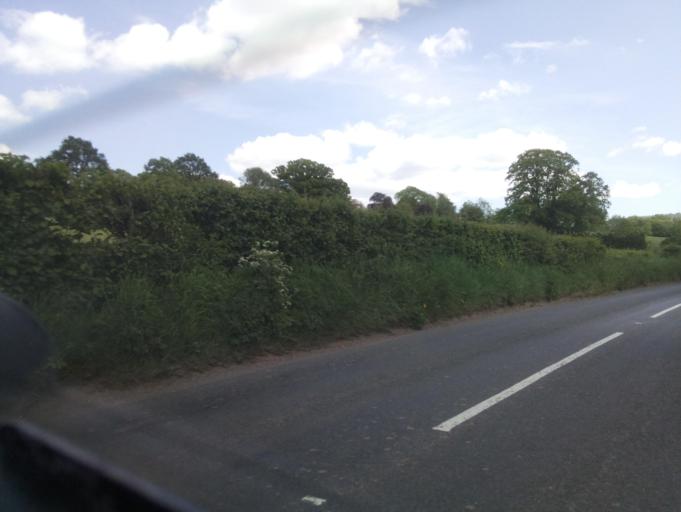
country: GB
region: Wales
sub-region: Monmouthshire
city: Monmouth
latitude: 51.8195
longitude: -2.7351
